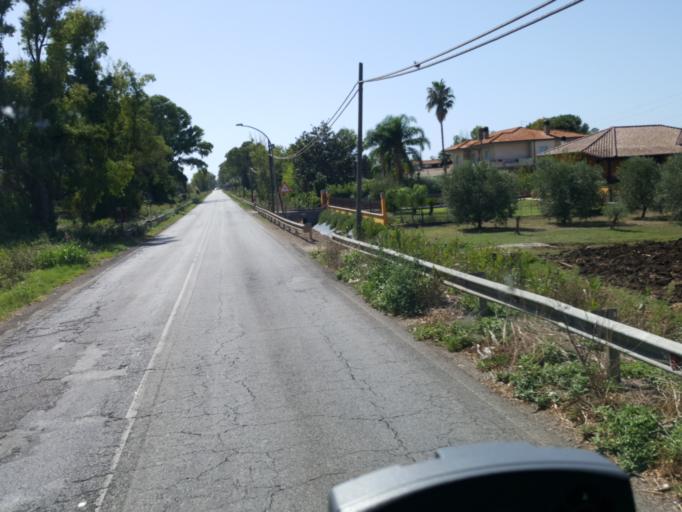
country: IT
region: Latium
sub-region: Provincia di Latina
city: Borgo Hermada
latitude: 41.3694
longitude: 13.1228
